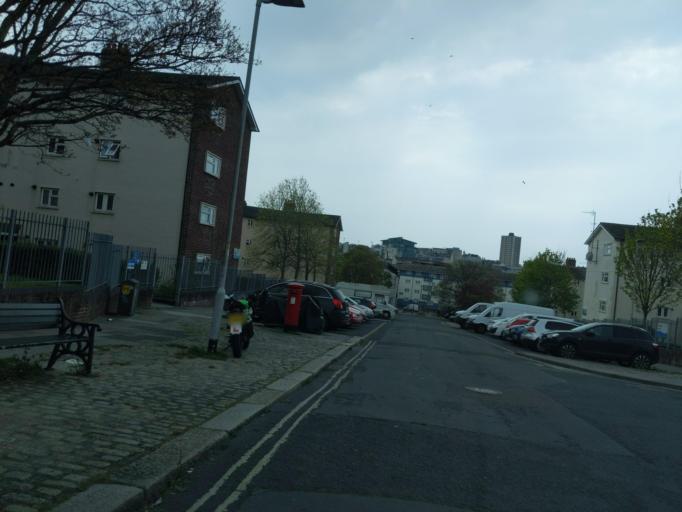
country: GB
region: England
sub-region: Plymouth
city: Plymouth
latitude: 50.3731
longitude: -4.1506
